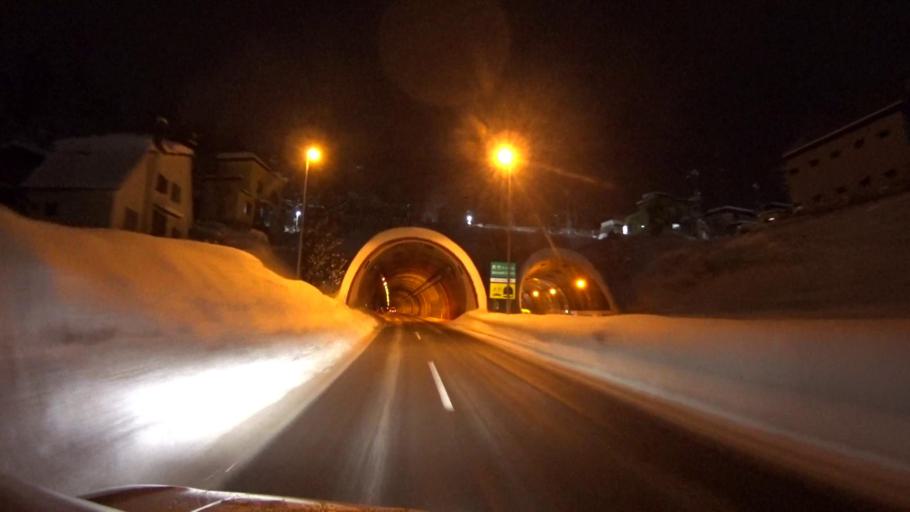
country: JP
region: Hokkaido
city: Otaru
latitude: 43.1765
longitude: 141.0261
